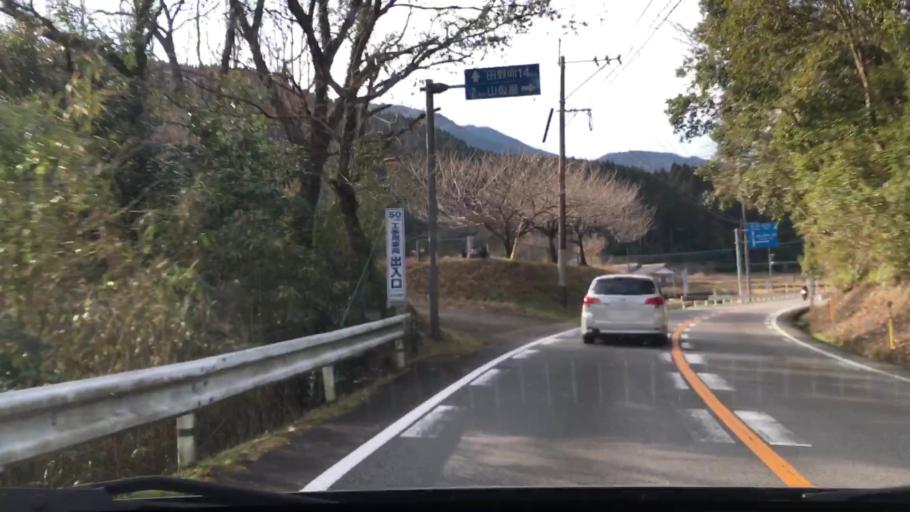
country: JP
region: Miyazaki
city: Nichinan
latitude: 31.7444
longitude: 131.3376
